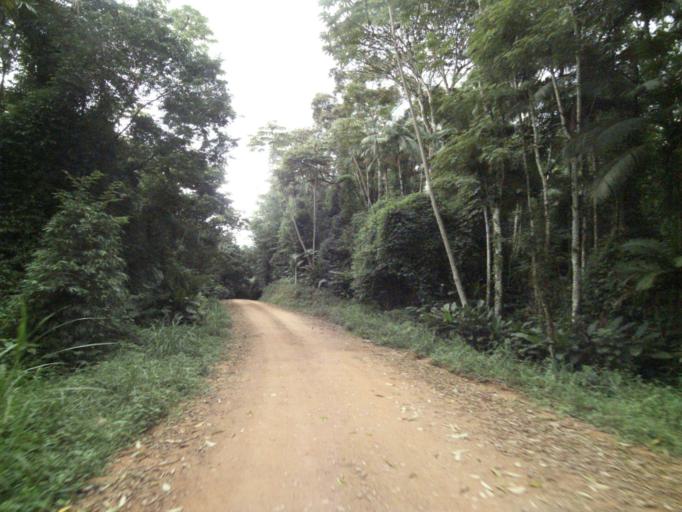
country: BR
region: Santa Catarina
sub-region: Pomerode
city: Pomerode
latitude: -26.7315
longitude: -49.1970
